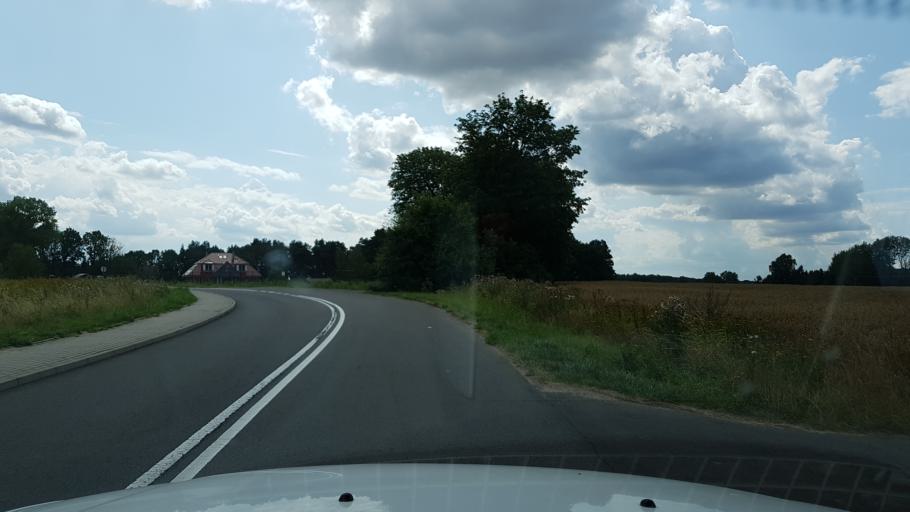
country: PL
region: West Pomeranian Voivodeship
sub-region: Powiat gryficki
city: Pobierowo
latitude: 54.0360
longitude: 14.8735
